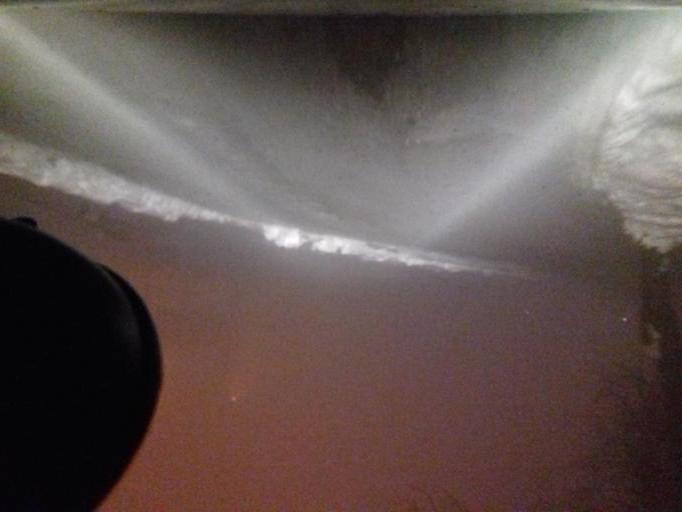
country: BA
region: Federation of Bosnia and Herzegovina
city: Kobilja Glava
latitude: 43.8676
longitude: 18.4124
